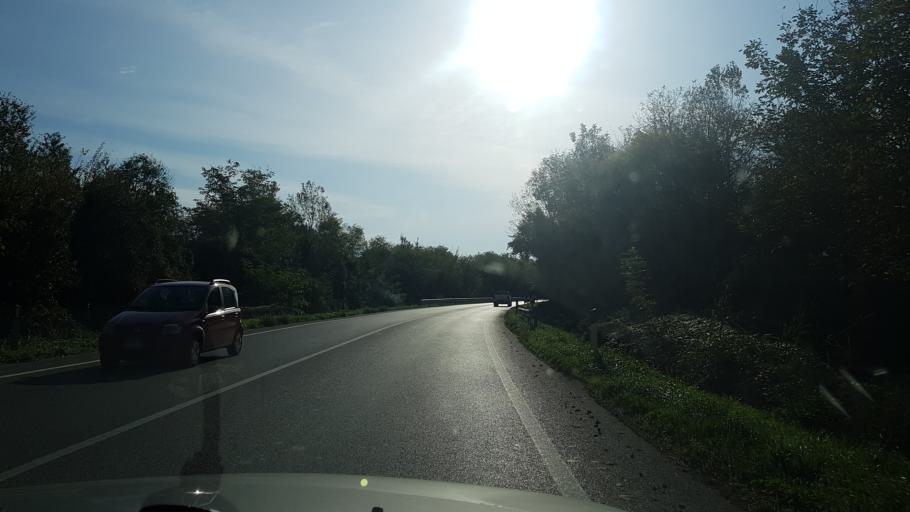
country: IT
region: Friuli Venezia Giulia
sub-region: Provincia di Udine
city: Artegna
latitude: 46.2431
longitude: 13.1373
